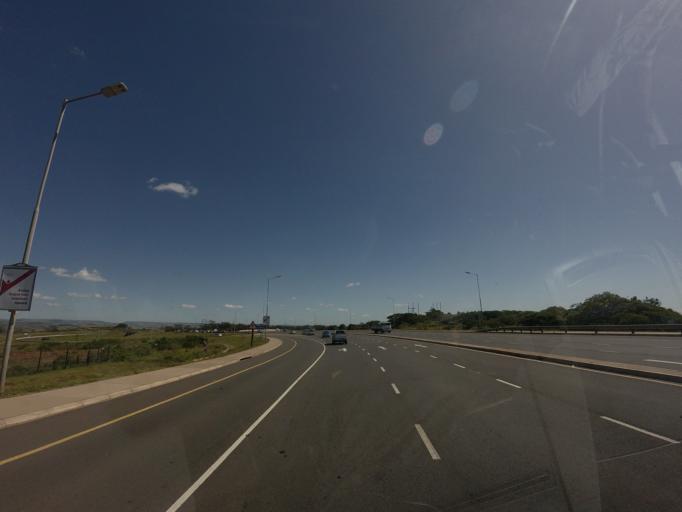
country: ZA
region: KwaZulu-Natal
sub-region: iLembe District Municipality
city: Ballitoville
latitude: -29.5205
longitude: 31.2014
